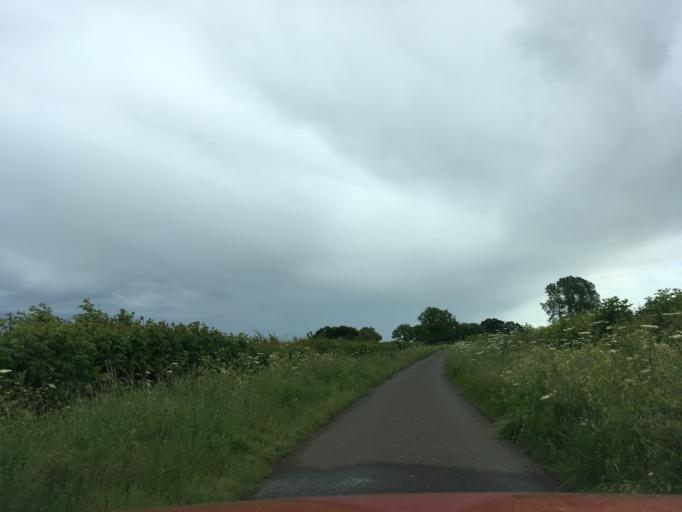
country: GB
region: England
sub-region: Wiltshire
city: Norton
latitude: 51.5903
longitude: -2.2034
